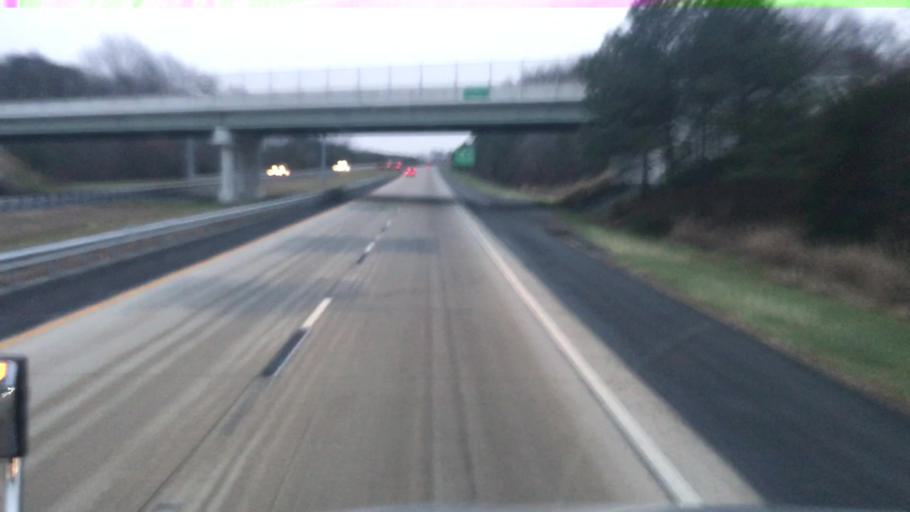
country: US
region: Delaware
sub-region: Kent County
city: Dover
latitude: 39.1770
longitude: -75.5032
